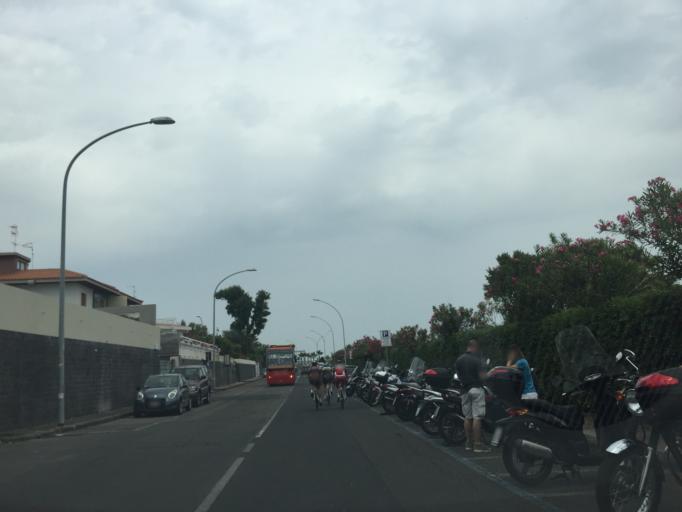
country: IT
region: Sicily
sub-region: Catania
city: Aci Castello
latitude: 37.5437
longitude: 15.1418
